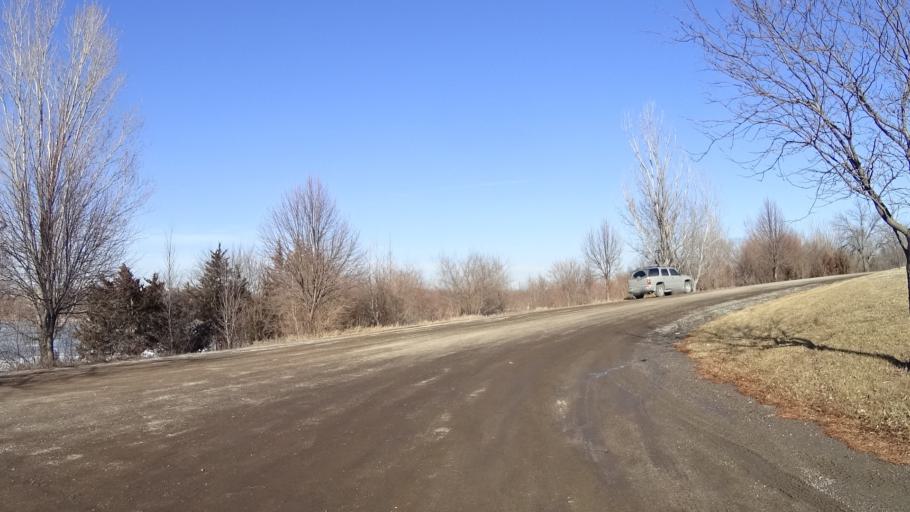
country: US
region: Nebraska
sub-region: Douglas County
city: Bennington
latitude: 41.3125
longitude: -96.1335
